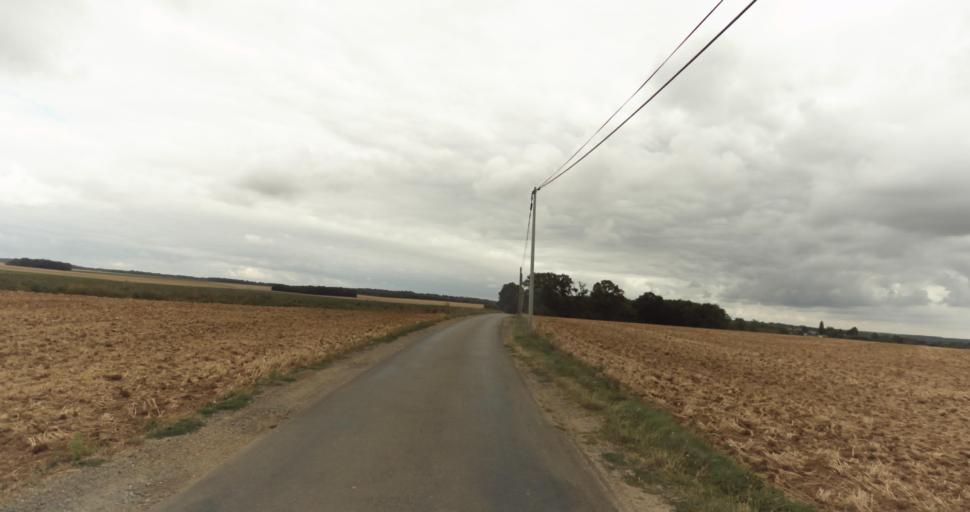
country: FR
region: Haute-Normandie
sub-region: Departement de l'Eure
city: Menilles
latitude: 49.0143
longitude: 1.3006
